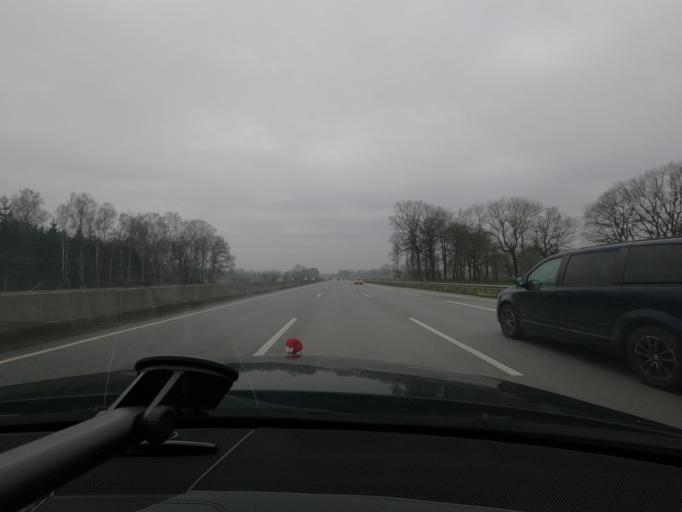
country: DE
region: Schleswig-Holstein
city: Bonningstedt
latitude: 53.6679
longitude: 9.9384
